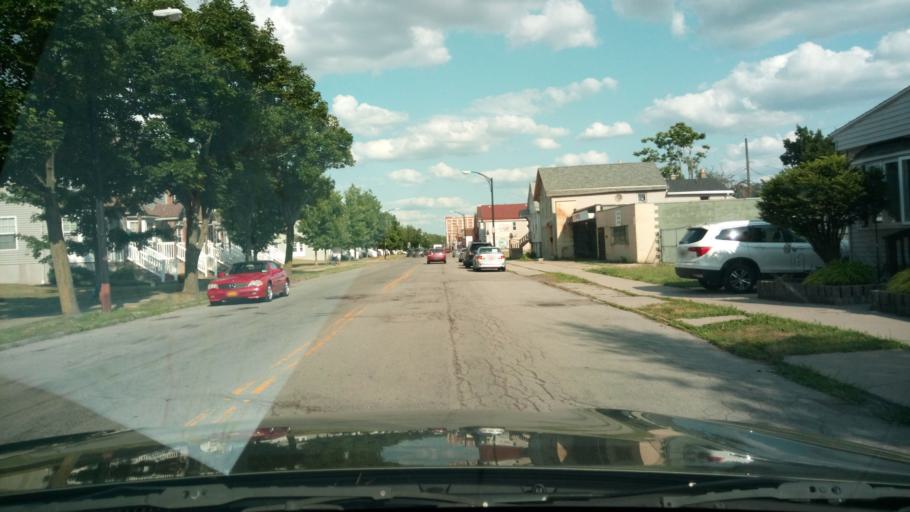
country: US
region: New York
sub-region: Erie County
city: Buffalo
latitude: 42.8799
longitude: -78.8638
